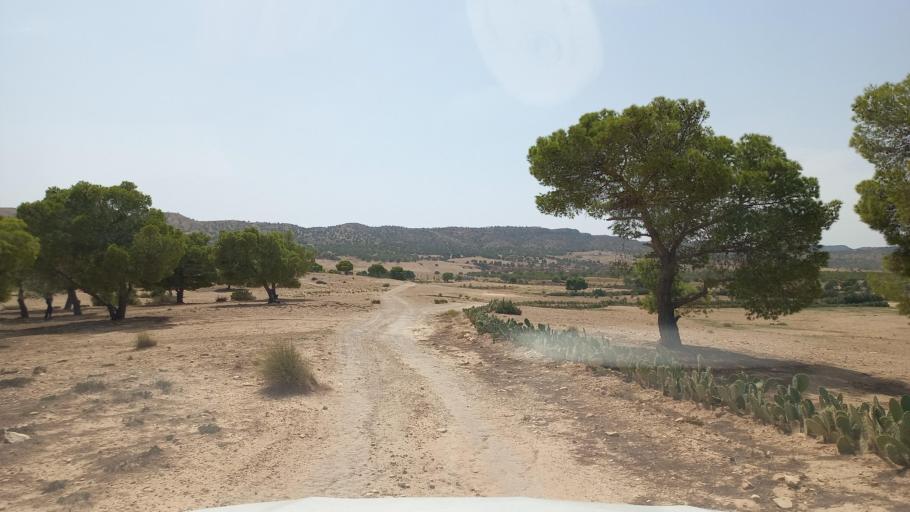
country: TN
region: Al Qasrayn
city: Sbiba
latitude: 35.3973
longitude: 8.9860
